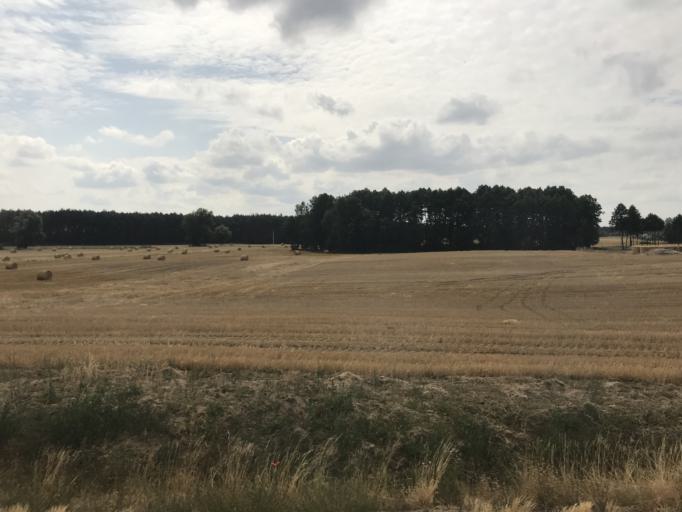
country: PL
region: Greater Poland Voivodeship
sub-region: Powiat gnieznienski
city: Trzemeszno
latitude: 52.5468
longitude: 17.7430
